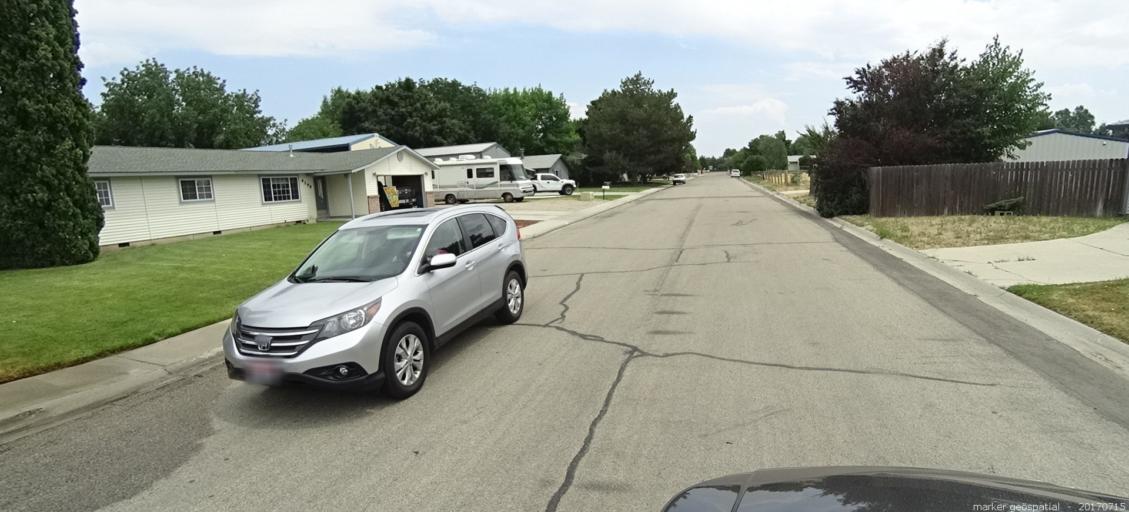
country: US
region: Idaho
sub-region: Ada County
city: Garden City
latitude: 43.5562
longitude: -116.2986
